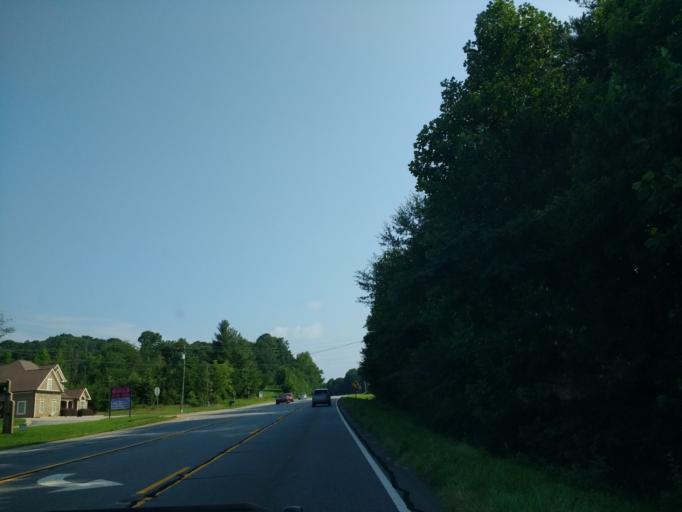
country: US
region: Georgia
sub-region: White County
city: Cleveland
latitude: 34.5214
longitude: -83.7550
